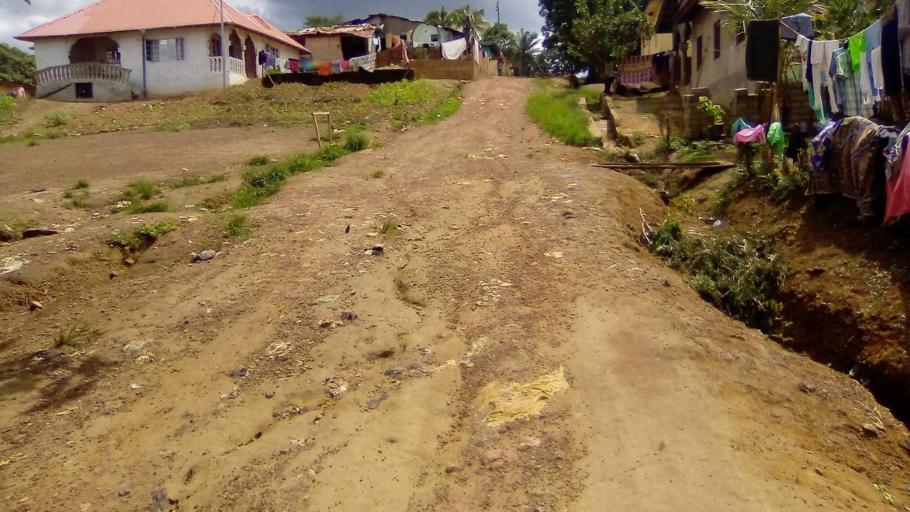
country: SL
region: Southern Province
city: Bo
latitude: 7.9624
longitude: -11.7209
